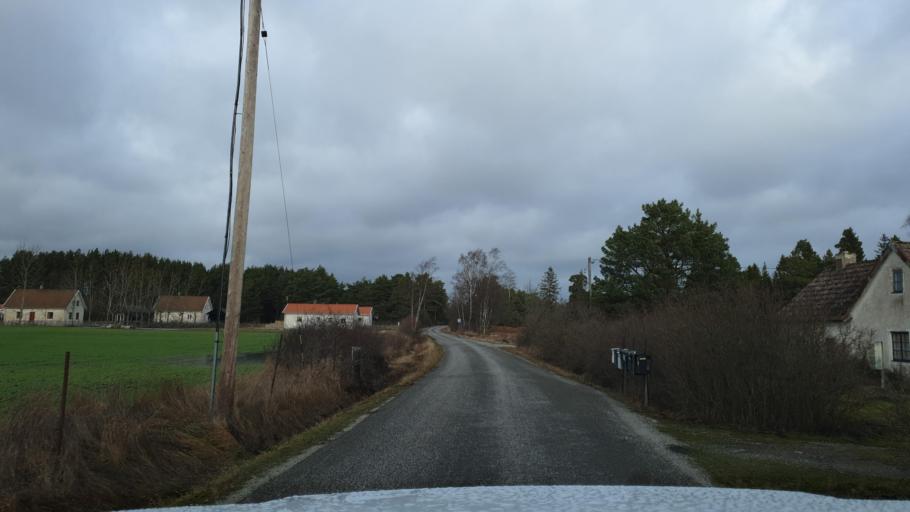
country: SE
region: Gotland
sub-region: Gotland
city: Slite
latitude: 57.3841
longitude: 18.8086
